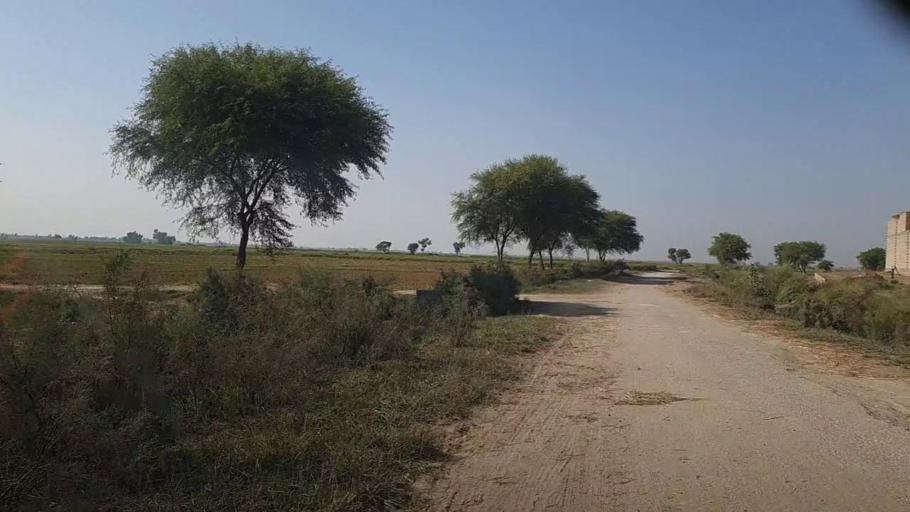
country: PK
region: Sindh
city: Tangwani
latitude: 28.2504
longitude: 68.9409
